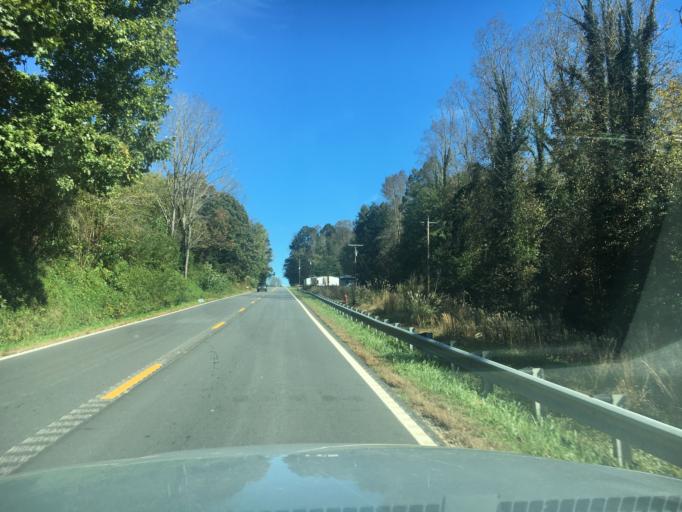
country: US
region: North Carolina
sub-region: Burke County
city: Salem
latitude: 35.6568
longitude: -81.7561
